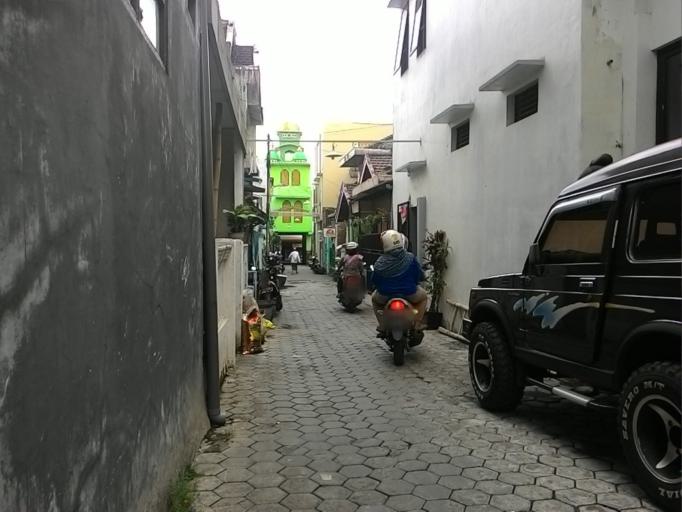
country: ID
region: East Java
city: Malang
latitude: -7.9463
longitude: 112.6110
